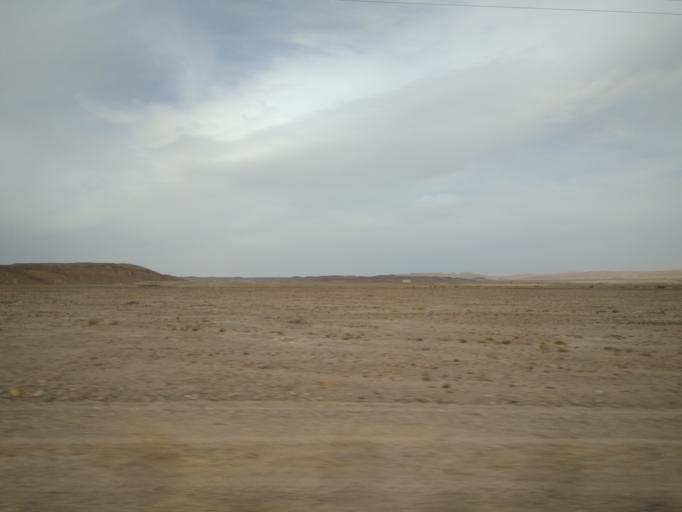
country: IL
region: Southern District
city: Eilat
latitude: 29.9564
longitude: 34.9259
